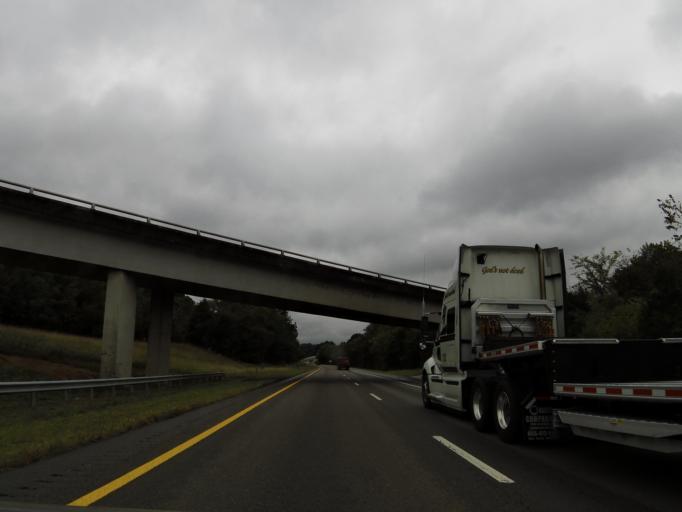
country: US
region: Tennessee
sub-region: Loudon County
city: Loudon
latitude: 35.7644
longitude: -84.3643
